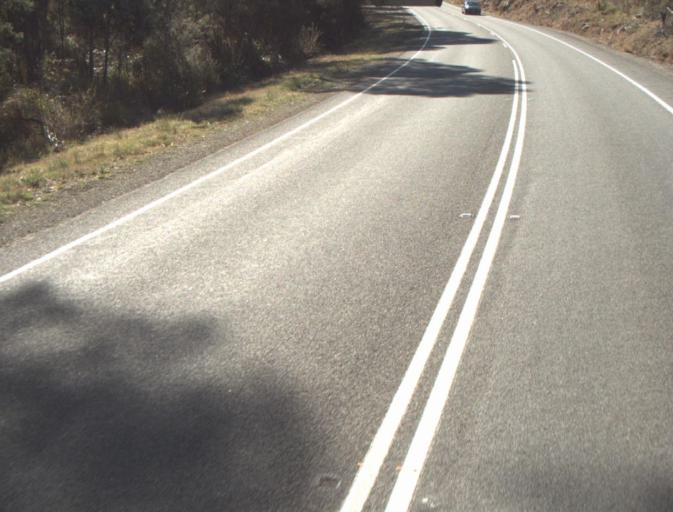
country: AU
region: Tasmania
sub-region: Launceston
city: Mayfield
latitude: -41.3532
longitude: 147.1438
